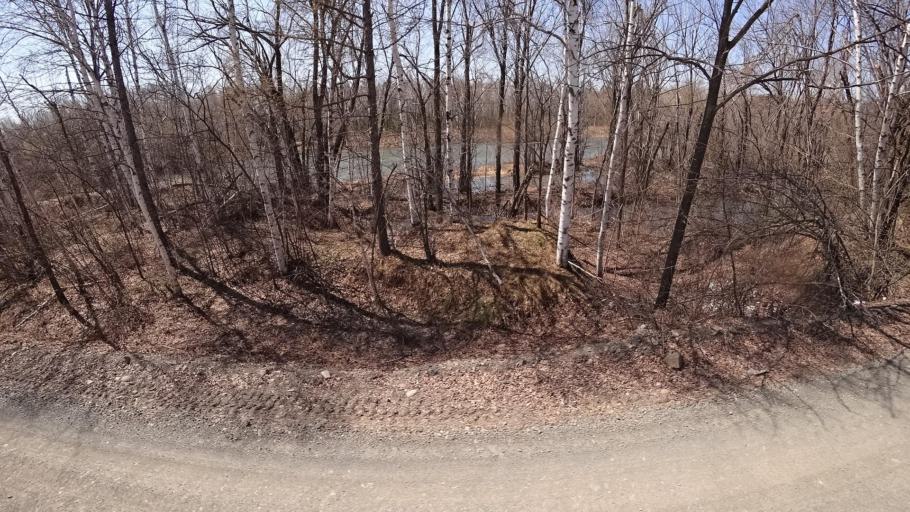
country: RU
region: Khabarovsk Krai
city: Khurba
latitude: 50.4116
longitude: 136.8435
